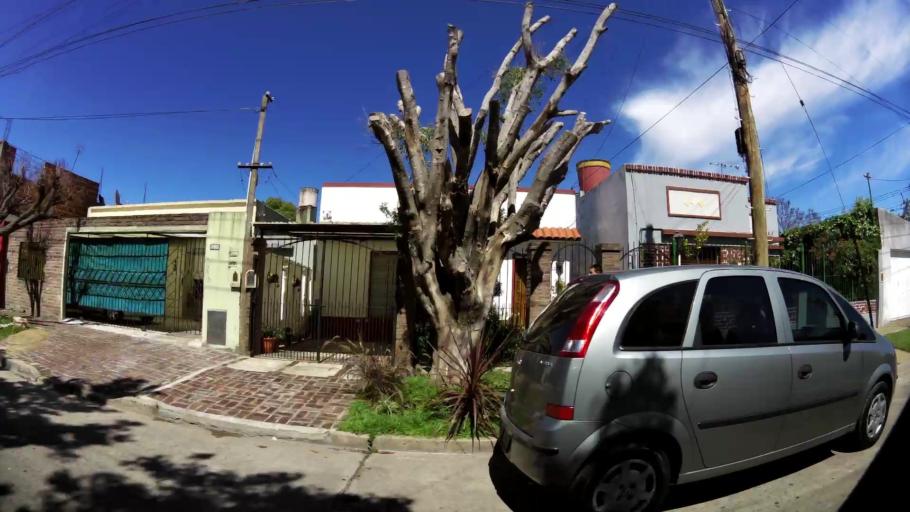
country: AR
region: Buenos Aires
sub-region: Partido de Quilmes
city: Quilmes
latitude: -34.7093
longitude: -58.2640
